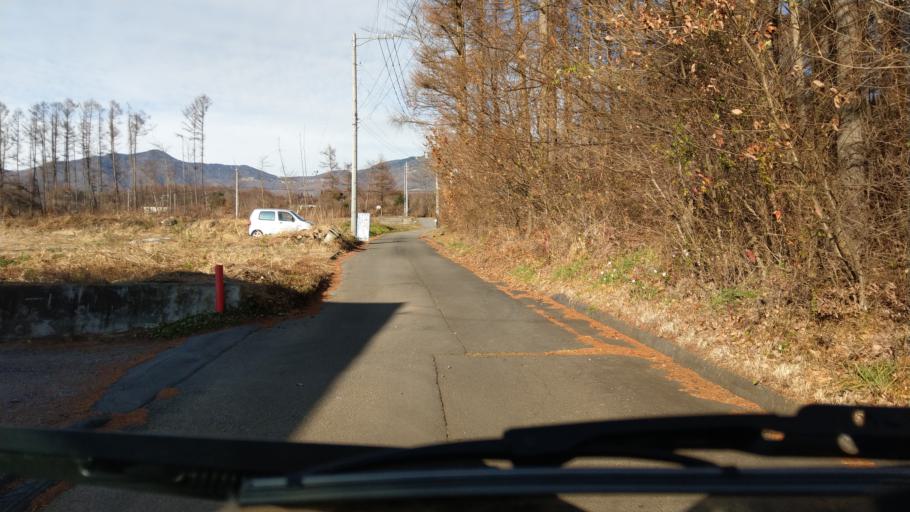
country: JP
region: Nagano
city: Komoro
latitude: 36.3423
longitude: 138.4620
